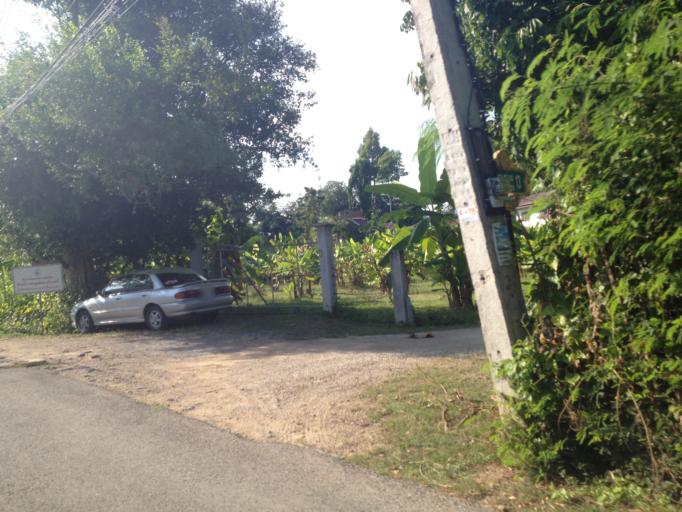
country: TH
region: Chiang Mai
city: Chiang Mai
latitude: 18.7440
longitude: 98.9508
